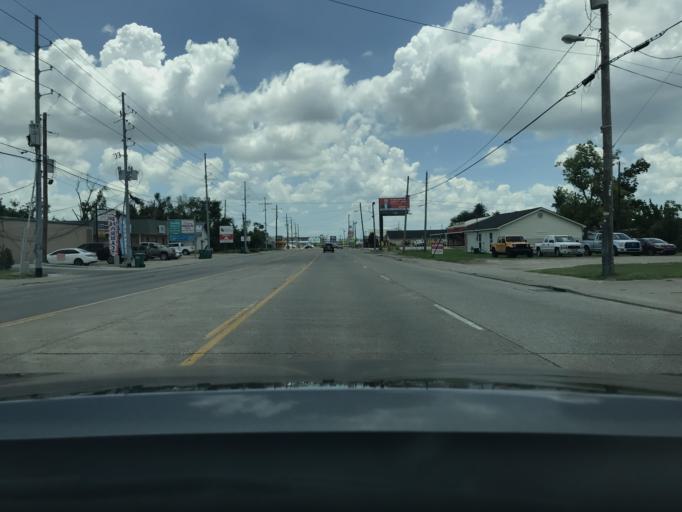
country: US
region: Louisiana
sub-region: Calcasieu Parish
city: Westlake
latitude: 30.2454
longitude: -93.2582
